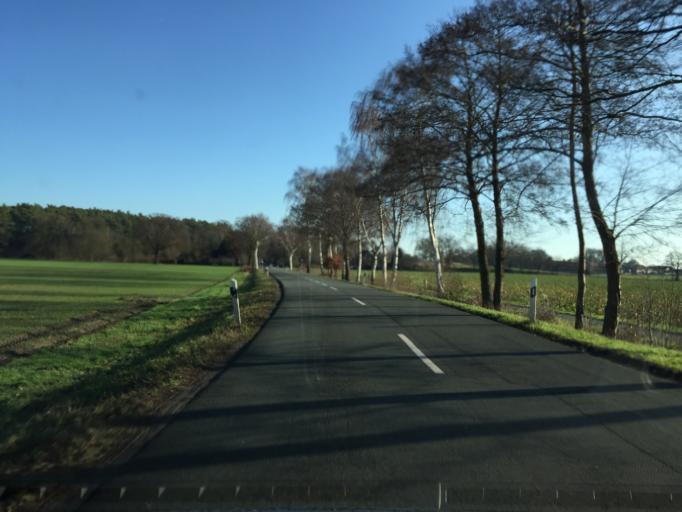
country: DE
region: Lower Saxony
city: Husum
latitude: 52.5487
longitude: 9.1985
